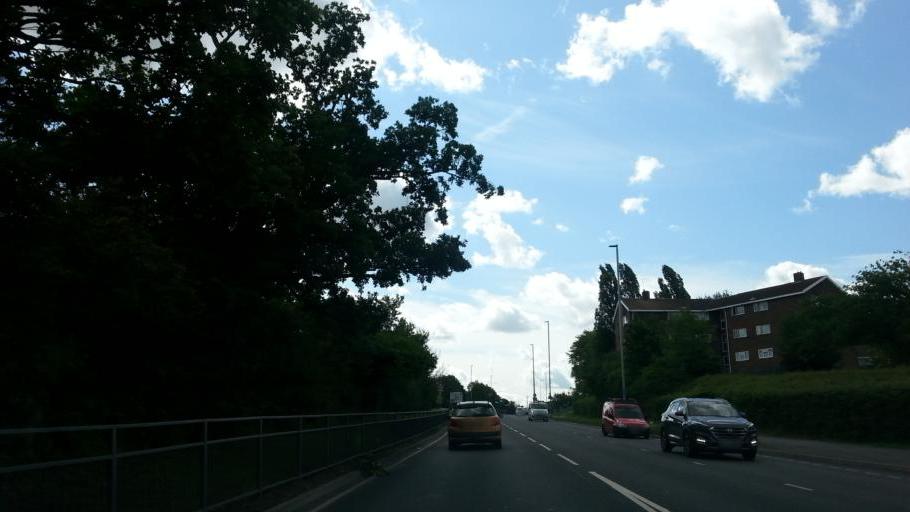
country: GB
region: England
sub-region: Essex
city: Basildon
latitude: 51.5643
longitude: 0.4529
